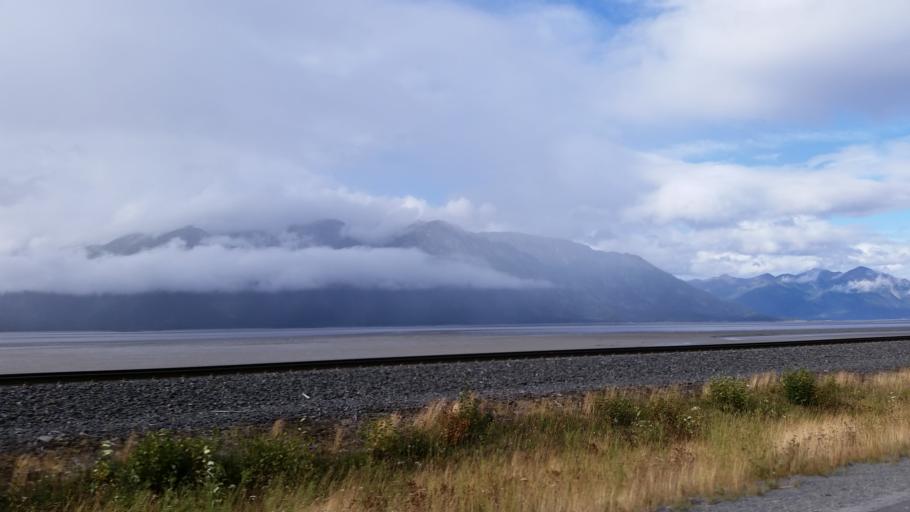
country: US
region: Alaska
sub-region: Anchorage Municipality
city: Girdwood
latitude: 60.9474
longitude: -149.3845
